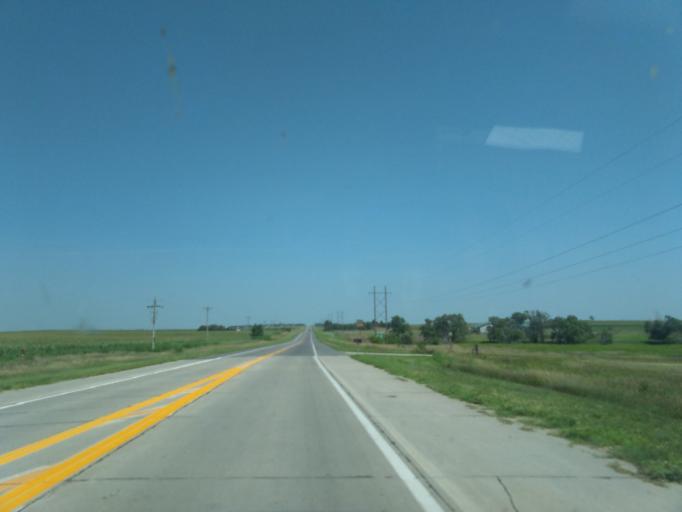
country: US
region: Nebraska
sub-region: Red Willow County
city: McCook
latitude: 40.2310
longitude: -100.6497
